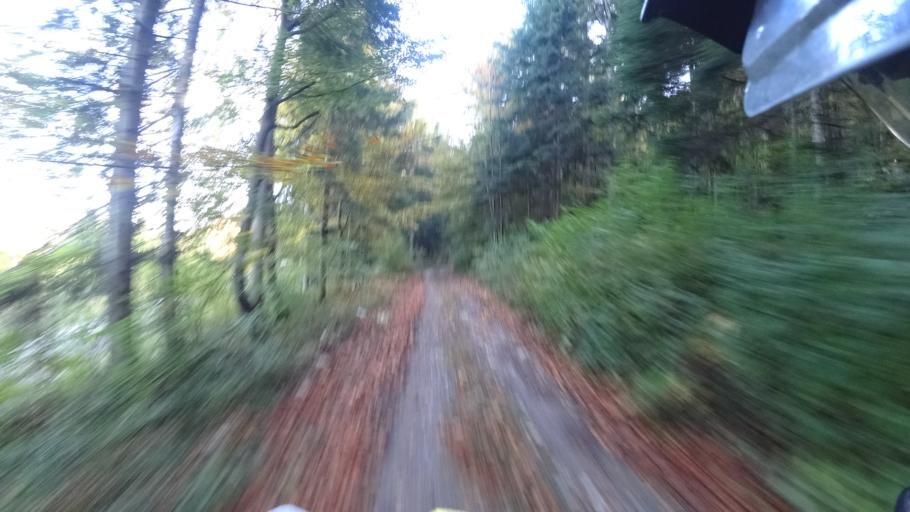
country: HR
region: Karlovacka
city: Plaski
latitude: 45.0153
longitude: 15.3970
